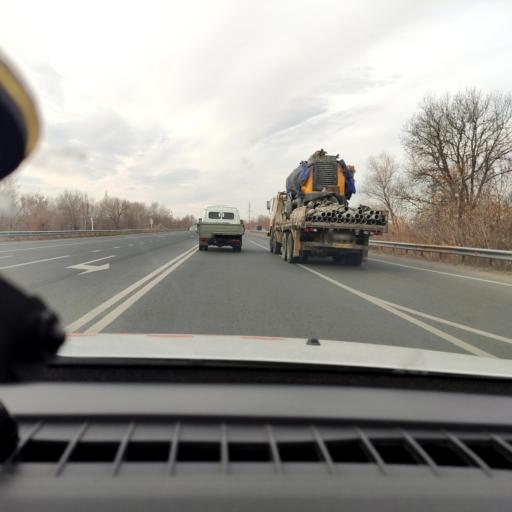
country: RU
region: Samara
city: Novokuybyshevsk
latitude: 53.1377
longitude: 49.9749
